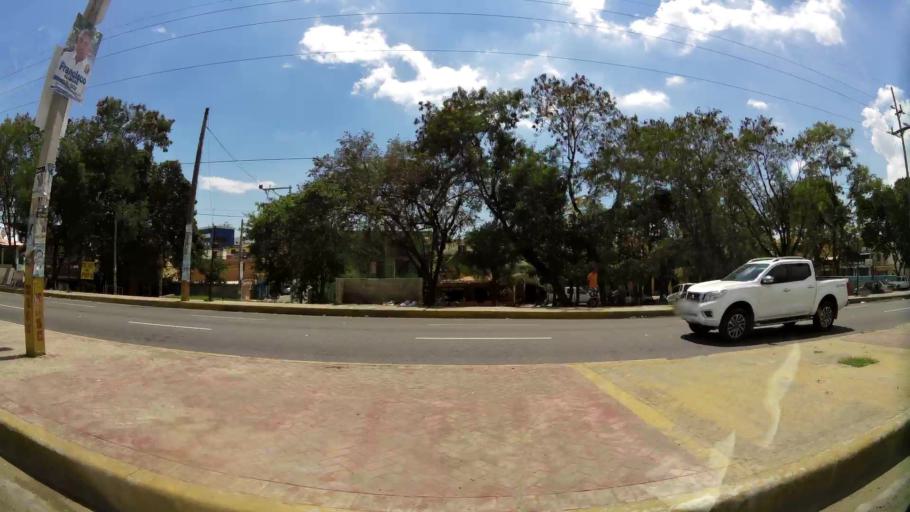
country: DO
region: Santo Domingo
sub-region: Santo Domingo
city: Santo Domingo Este
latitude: 18.5428
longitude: -69.8621
